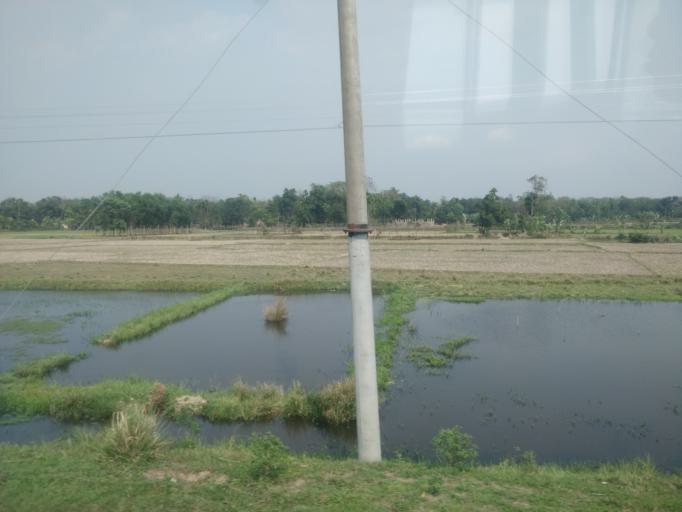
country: BD
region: Sylhet
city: Habiganj
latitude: 24.3222
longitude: 91.4342
